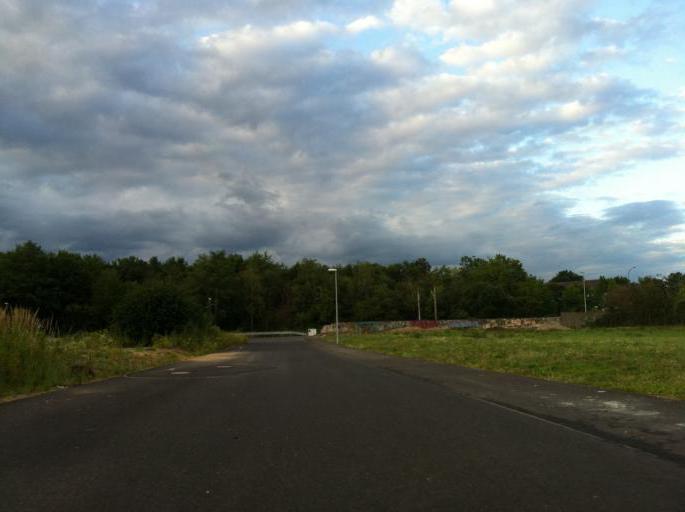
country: DE
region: North Rhine-Westphalia
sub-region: Regierungsbezirk Koln
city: Poll
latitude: 50.9049
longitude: 7.0157
